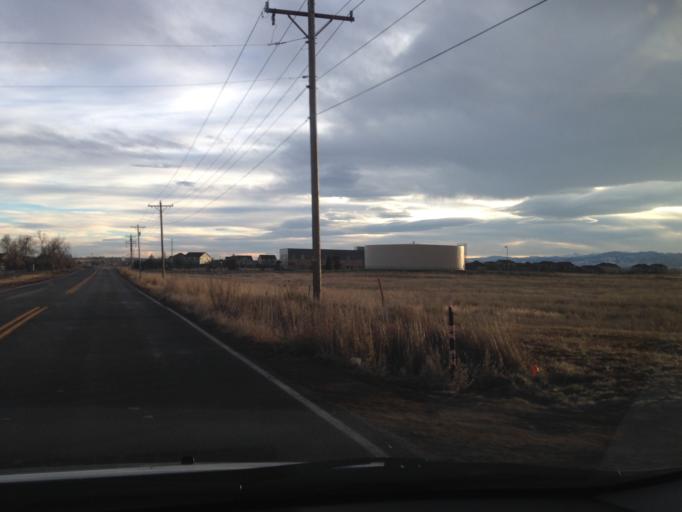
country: US
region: Colorado
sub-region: Weld County
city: Dacono
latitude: 40.0991
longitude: -104.9989
